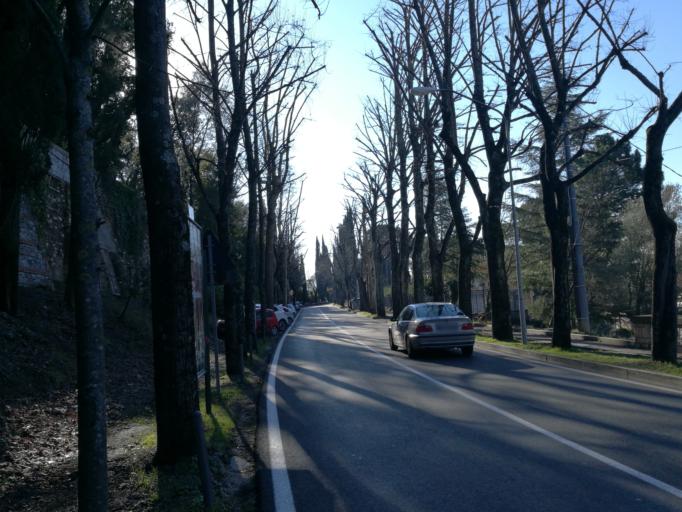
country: IT
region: Umbria
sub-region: Provincia di Perugia
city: Perugia
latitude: 43.1012
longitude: 12.3946
